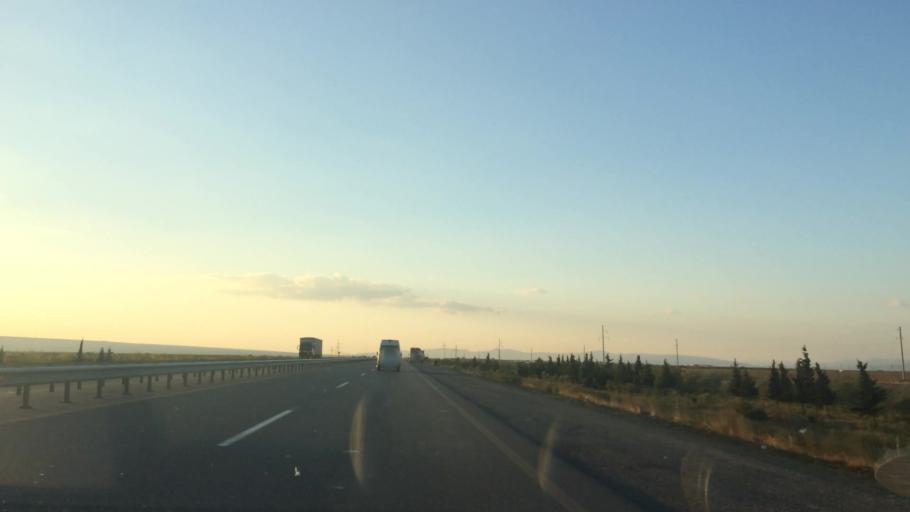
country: AZ
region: Baki
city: Qobustan
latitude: 39.9929
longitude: 49.1925
